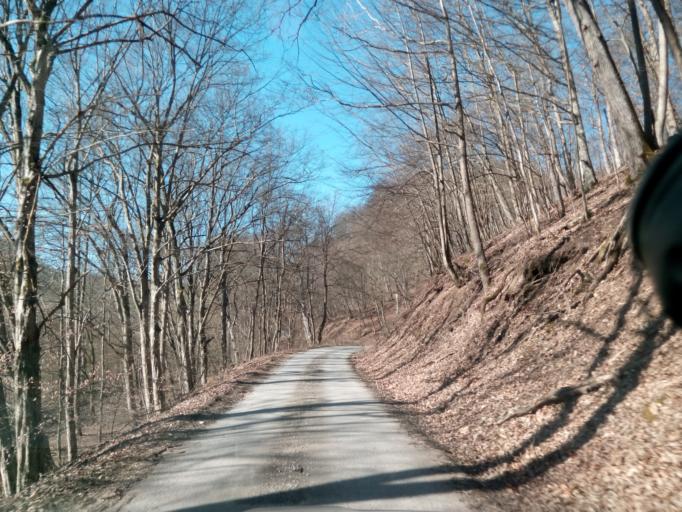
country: SK
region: Kosicky
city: Roznava
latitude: 48.5517
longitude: 20.5855
